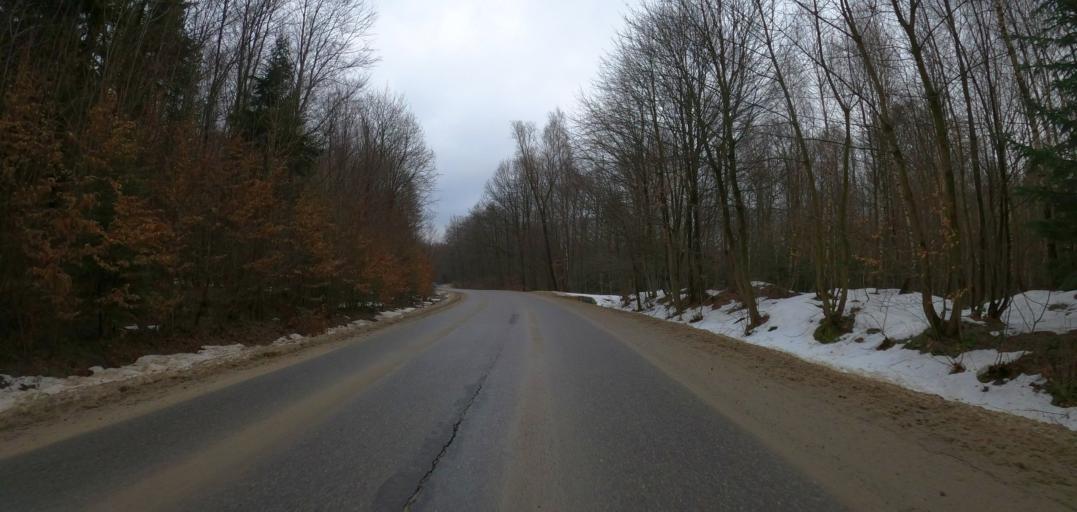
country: PL
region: Subcarpathian Voivodeship
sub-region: Powiat debicki
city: Debica
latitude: 49.9823
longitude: 21.4098
